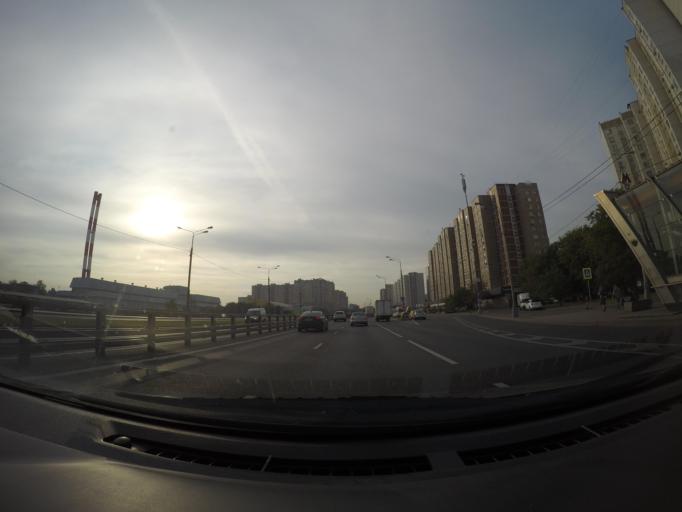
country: RU
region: Moscow
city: Zhulebino
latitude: 55.7019
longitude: 37.8506
